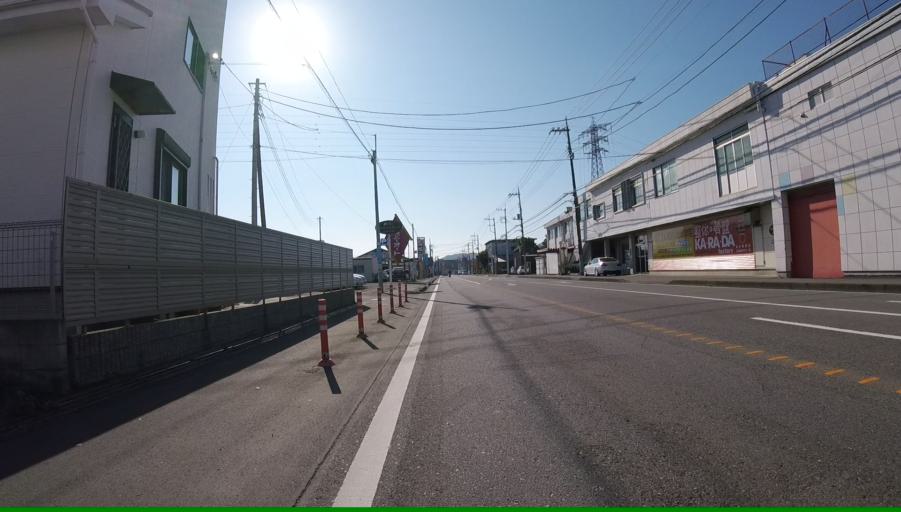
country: JP
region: Shizuoka
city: Mishima
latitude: 35.1071
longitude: 138.9158
